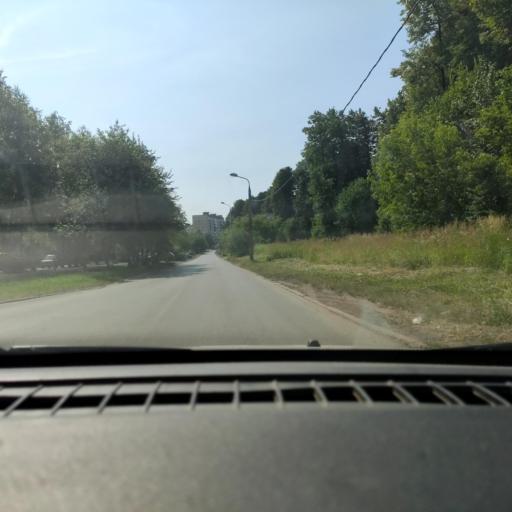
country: RU
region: Perm
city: Perm
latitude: 58.0890
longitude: 56.4117
